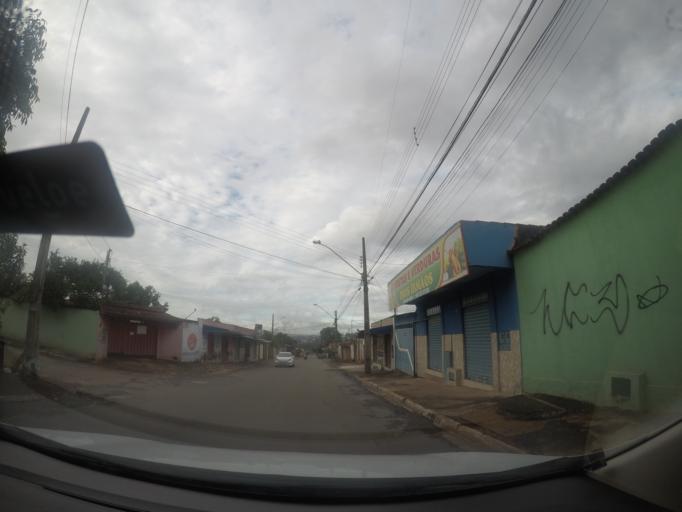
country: BR
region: Goias
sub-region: Goiania
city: Goiania
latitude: -16.6094
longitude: -49.3318
